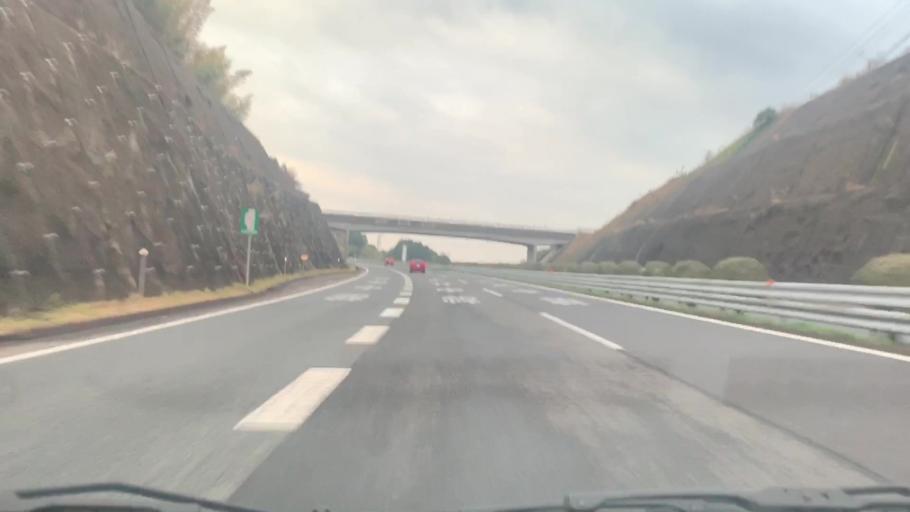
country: JP
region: Nagasaki
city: Omura
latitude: 32.9974
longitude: 129.9512
